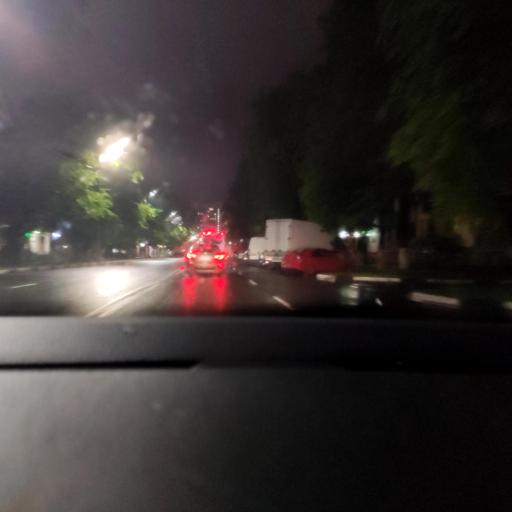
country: RU
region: Moskovskaya
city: Balashikha
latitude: 55.7991
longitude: 37.9346
